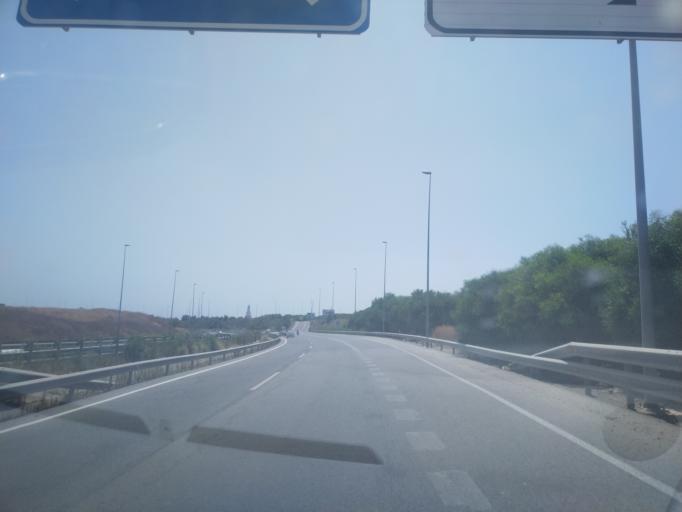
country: ES
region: Andalusia
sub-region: Provincia de Cadiz
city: Chiclana de la Frontera
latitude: 36.4031
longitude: -6.1265
